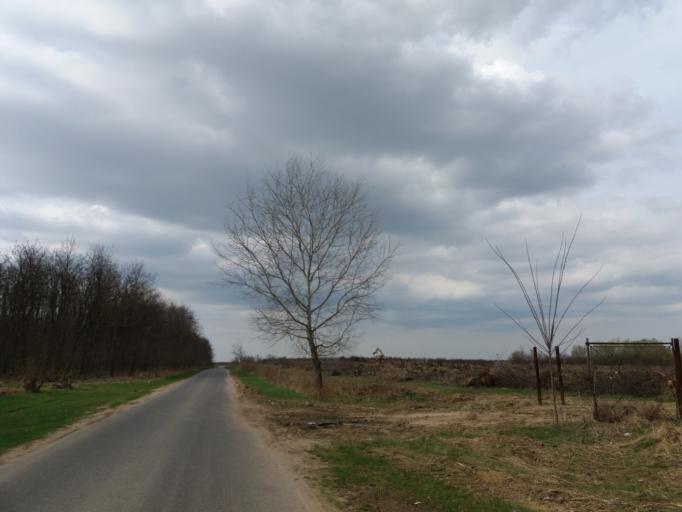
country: HU
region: Szabolcs-Szatmar-Bereg
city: Nyirtass
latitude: 48.0886
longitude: 22.0349
